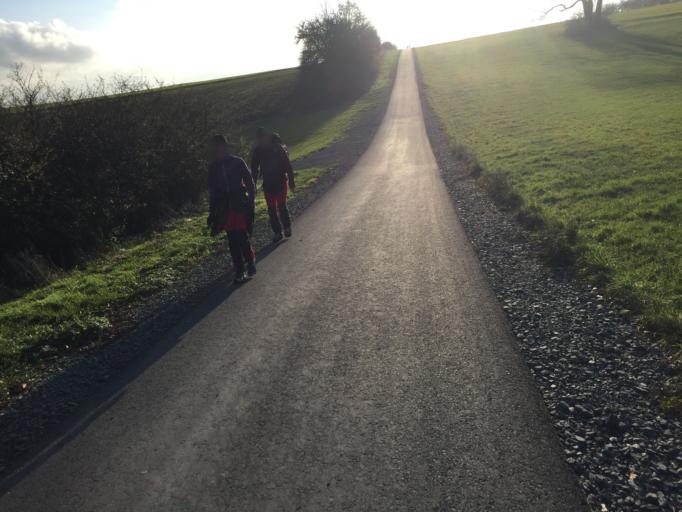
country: DE
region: Hesse
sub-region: Regierungsbezirk Giessen
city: Langgons
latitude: 50.5167
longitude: 8.7128
